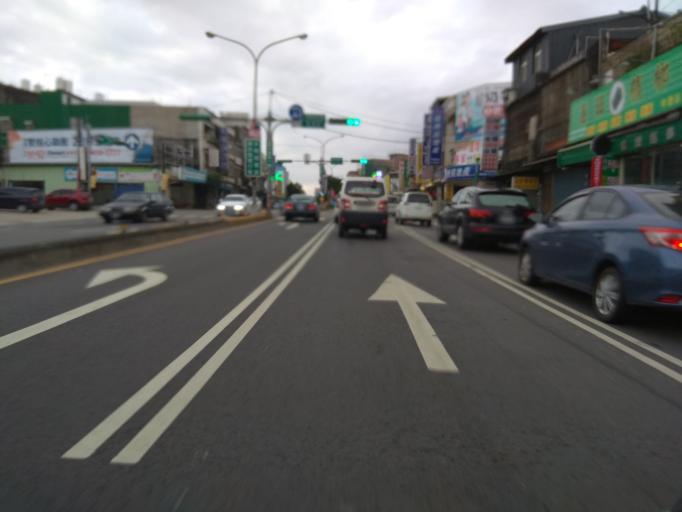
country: TW
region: Taiwan
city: Daxi
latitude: 24.9333
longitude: 121.2149
